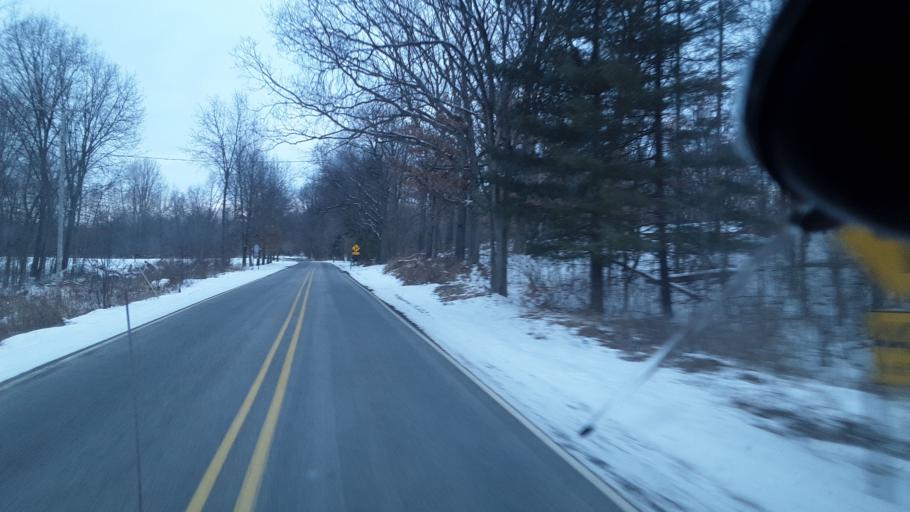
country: US
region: Michigan
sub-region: Ingham County
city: Leslie
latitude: 42.4454
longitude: -84.3261
